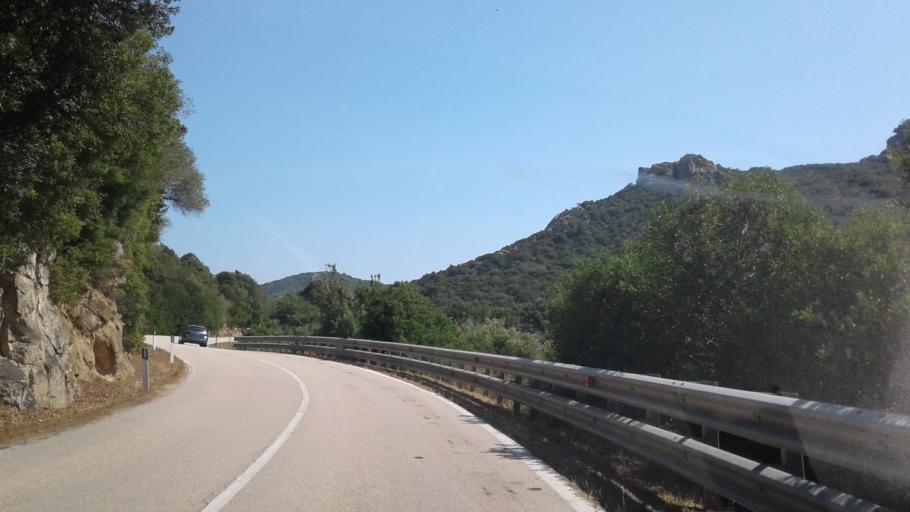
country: IT
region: Sardinia
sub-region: Provincia di Olbia-Tempio
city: Palau
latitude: 41.1393
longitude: 9.3086
